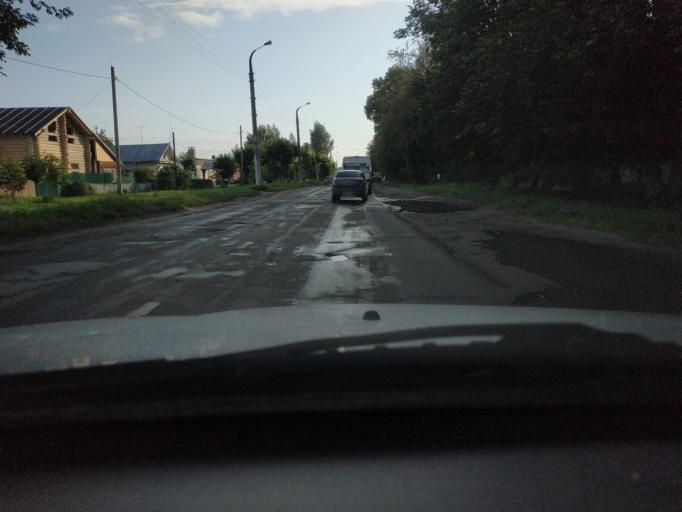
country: RU
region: Kostroma
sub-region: Kostromskoy Rayon
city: Kostroma
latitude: 57.7572
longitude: 40.8972
